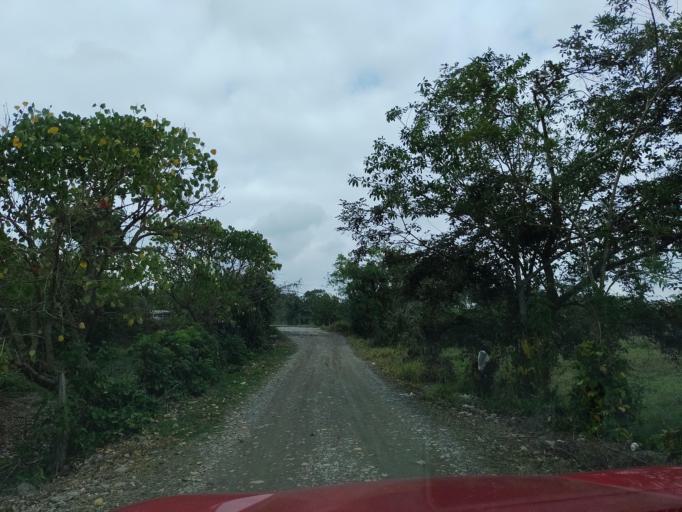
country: MX
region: Veracruz
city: Coatzintla
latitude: 20.4576
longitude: -97.4185
